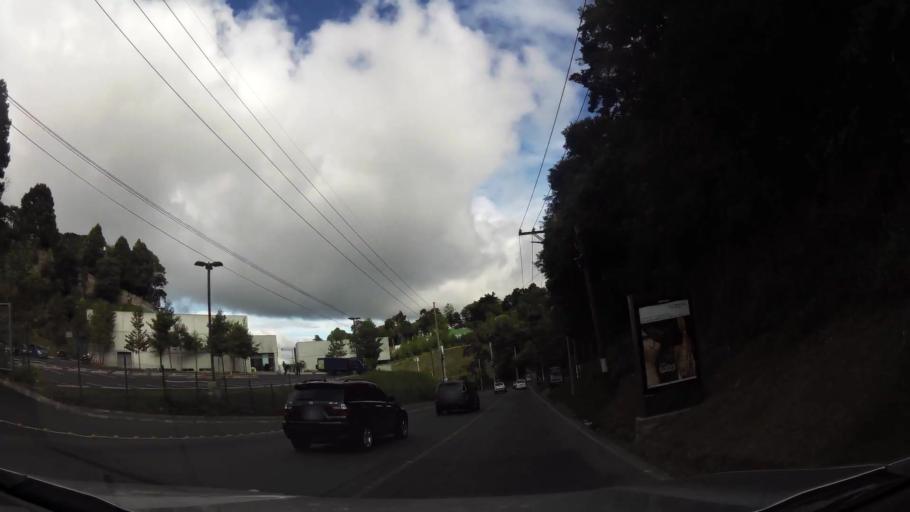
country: GT
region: Guatemala
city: Santa Catarina Pinula
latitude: 14.5652
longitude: -90.4810
